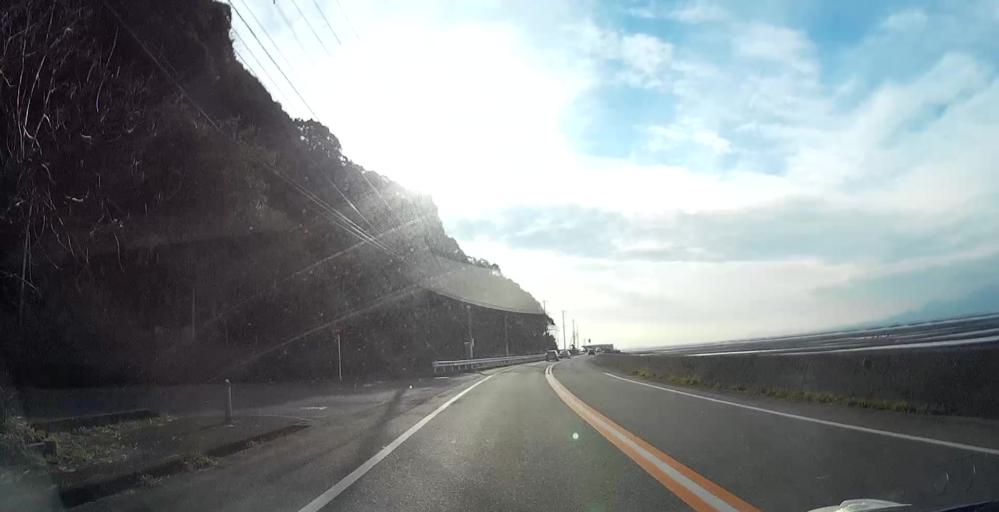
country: JP
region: Kumamoto
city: Uto
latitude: 32.6894
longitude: 130.5579
